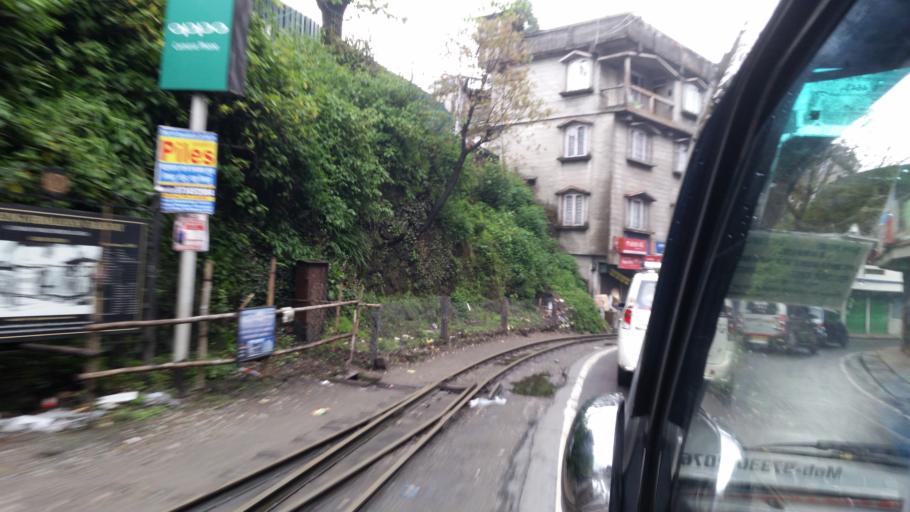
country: IN
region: West Bengal
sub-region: Darjiling
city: Darjiling
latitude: 27.0083
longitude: 88.2531
